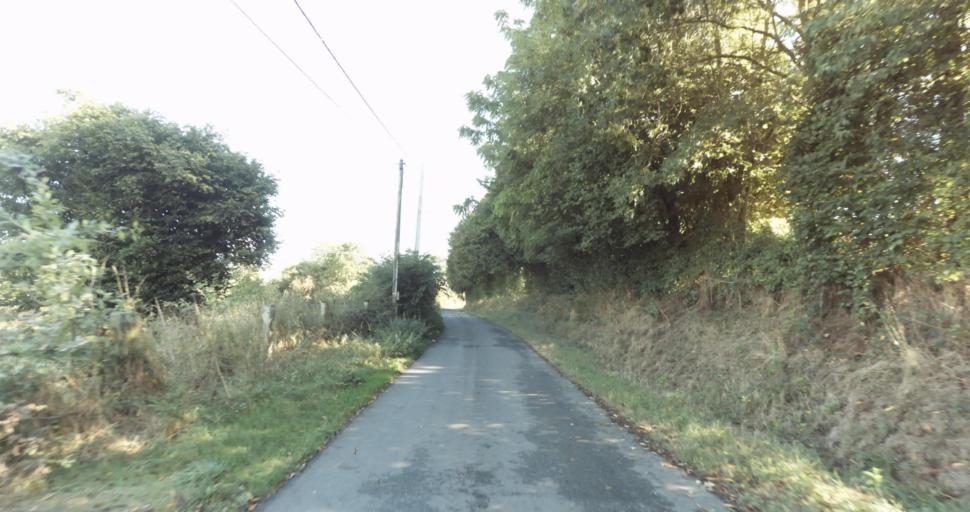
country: FR
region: Lower Normandy
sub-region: Departement de l'Orne
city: Vimoutiers
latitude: 48.9102
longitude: 0.1287
